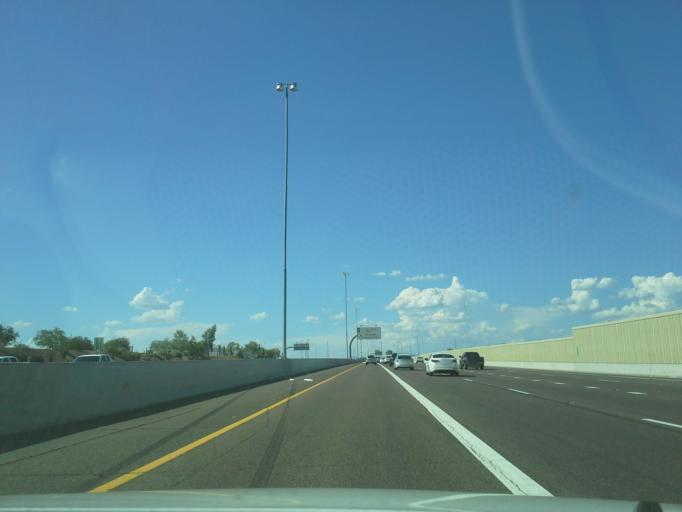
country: US
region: Arizona
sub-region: Maricopa County
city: Paradise Valley
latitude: 33.6603
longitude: -111.9997
